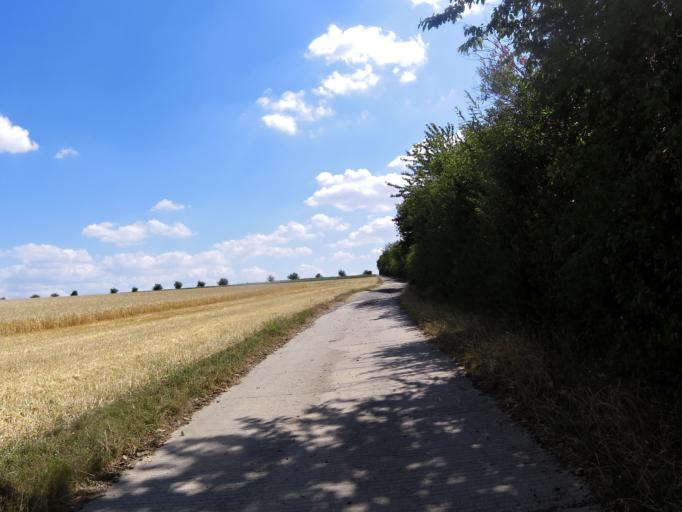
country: DE
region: Bavaria
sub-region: Regierungsbezirk Unterfranken
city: Wuerzburg
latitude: 49.8237
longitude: 9.9331
